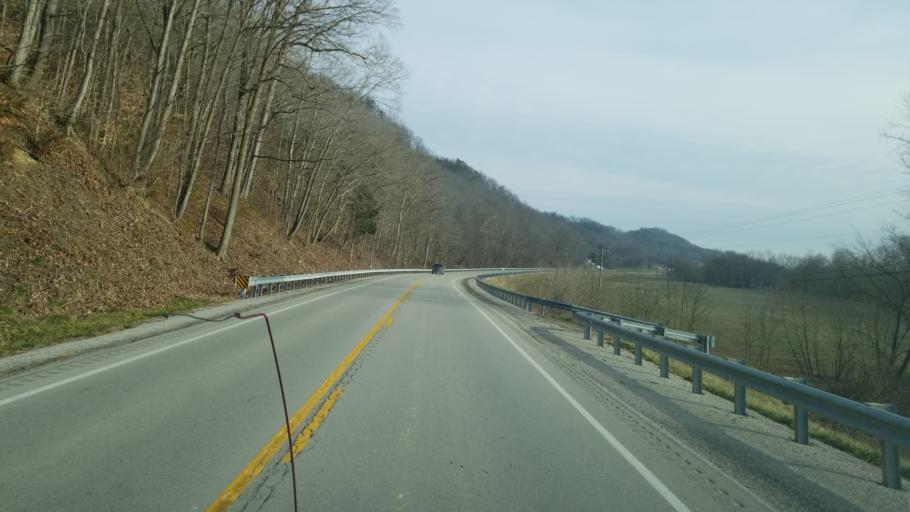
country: US
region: Kentucky
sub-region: Casey County
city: Liberty
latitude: 37.3412
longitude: -84.8988
